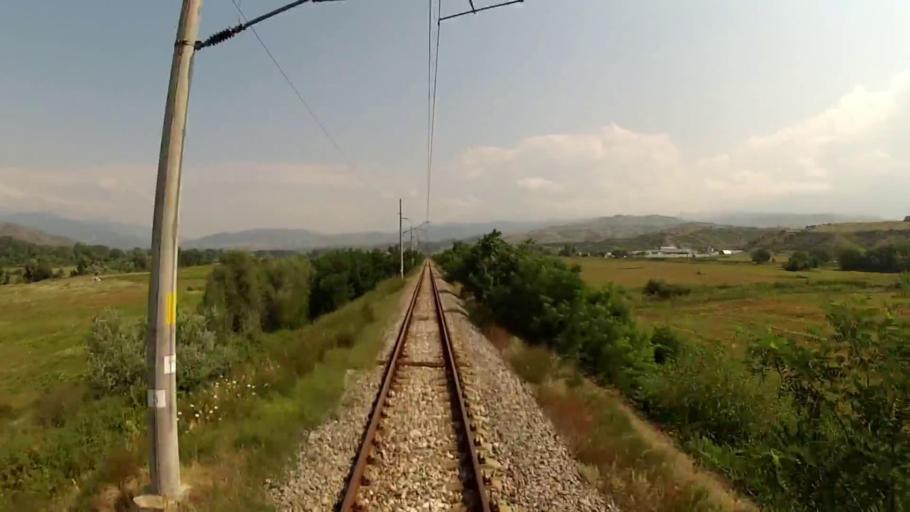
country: BG
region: Blagoevgrad
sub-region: Obshtina Strumyani
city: Strumyani
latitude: 41.6501
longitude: 23.1917
